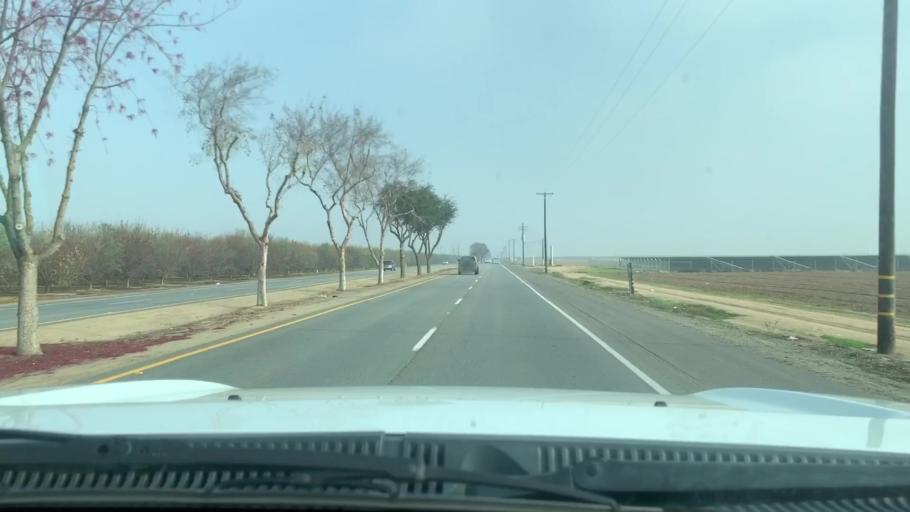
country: US
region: California
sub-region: Kern County
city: Shafter
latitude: 35.4997
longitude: -119.2362
